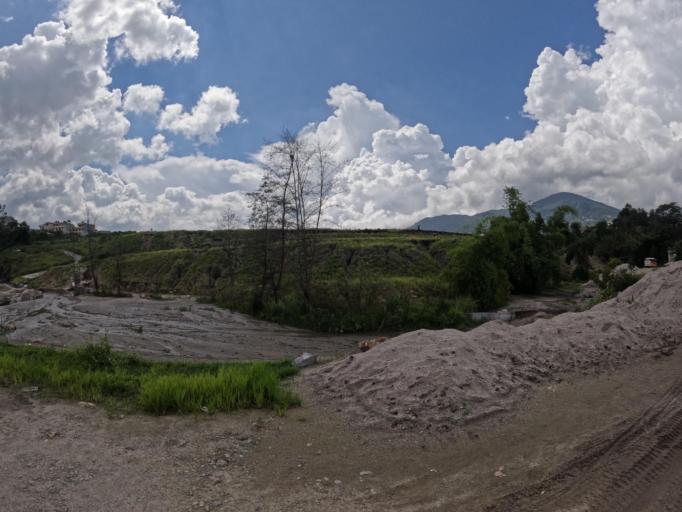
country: NP
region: Central Region
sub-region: Bagmati Zone
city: Kathmandu
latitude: 27.7806
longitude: 85.3276
